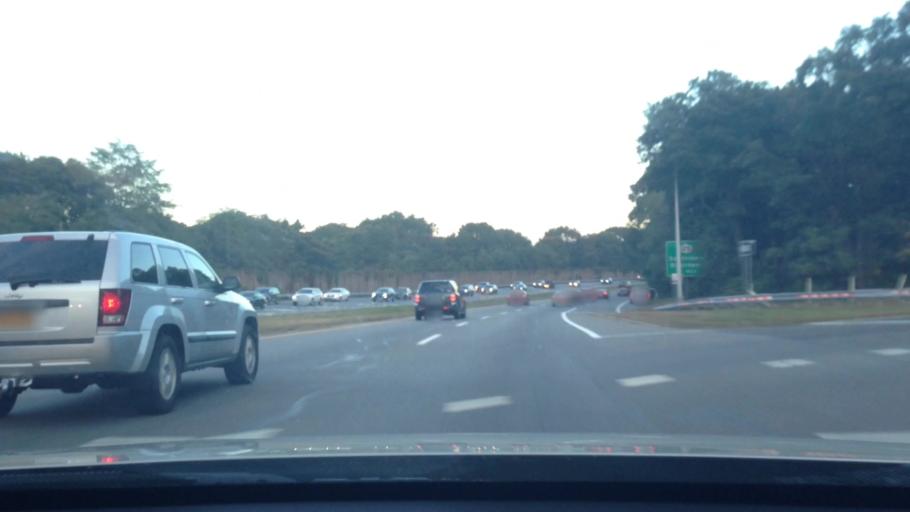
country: US
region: New York
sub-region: Suffolk County
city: Selden
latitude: 40.8503
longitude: -73.0639
